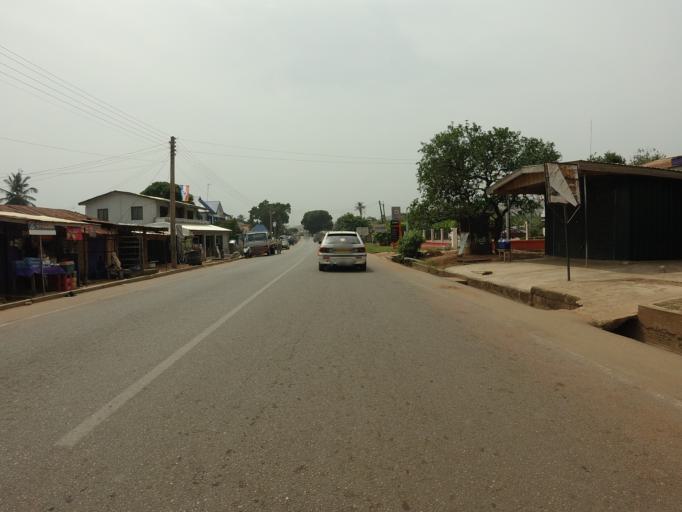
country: GH
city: Akropong
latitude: 6.0995
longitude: -0.0177
